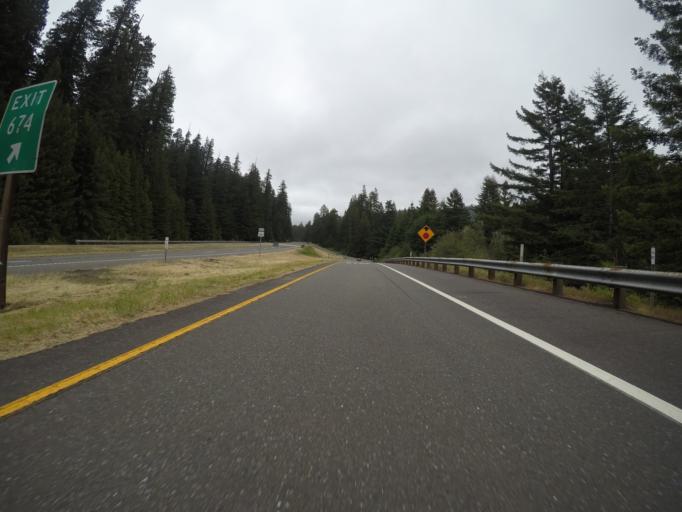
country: US
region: California
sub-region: Humboldt County
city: Rio Dell
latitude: 40.4397
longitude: -124.0341
